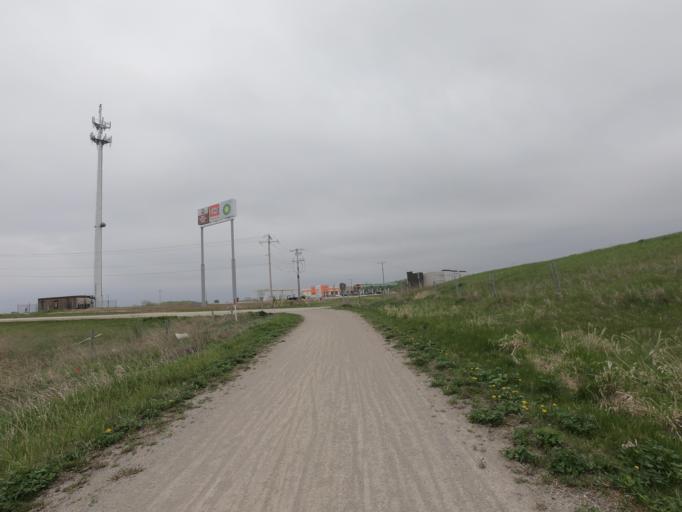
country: US
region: Wisconsin
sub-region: Jefferson County
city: Jefferson
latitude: 43.0324
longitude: -88.8038
